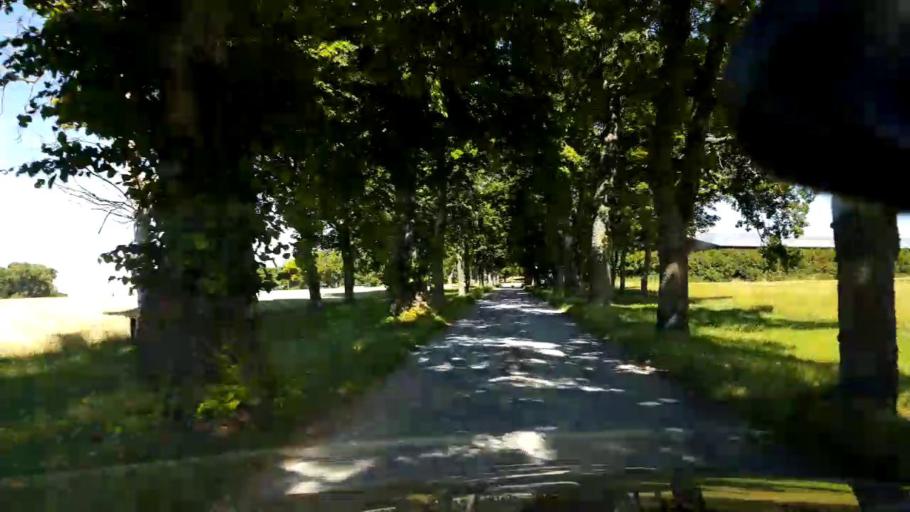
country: SE
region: Stockholm
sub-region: Sigtuna Kommun
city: Sigtuna
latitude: 59.6039
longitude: 17.6461
